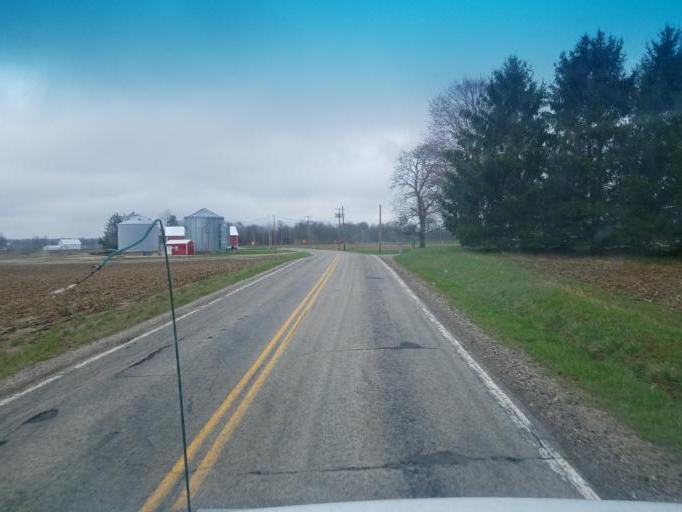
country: US
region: Ohio
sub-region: Richland County
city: Shelby
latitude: 40.9197
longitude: -82.6412
